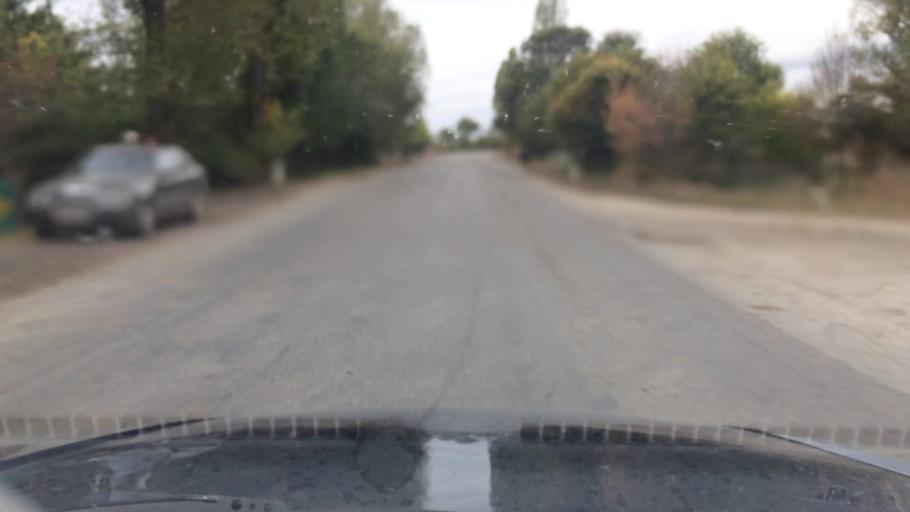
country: KG
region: Ysyk-Koel
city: Pokrovka
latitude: 42.7371
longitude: 77.9353
